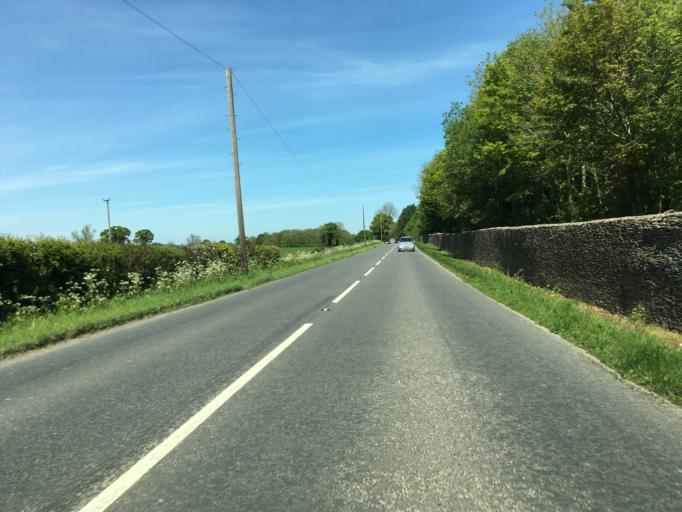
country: GB
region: England
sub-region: Wiltshire
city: Charlton
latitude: 51.6083
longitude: -2.0828
